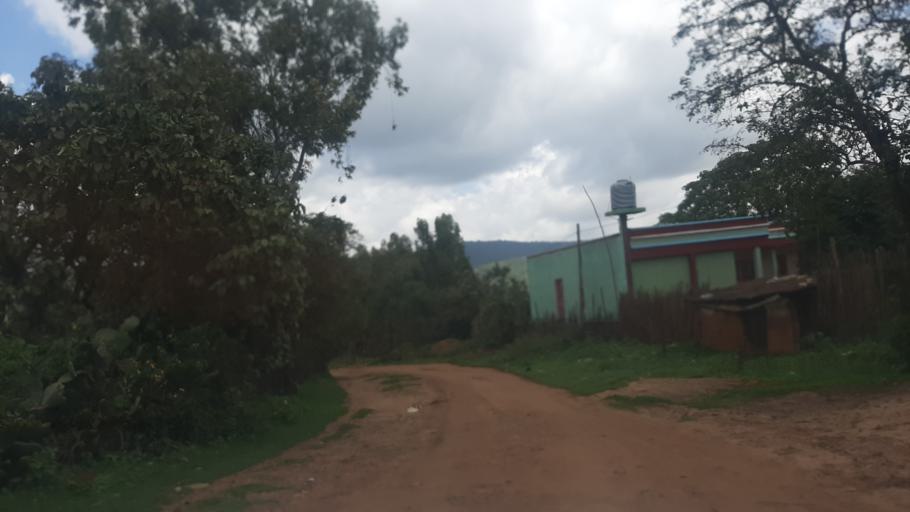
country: ET
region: Oromiya
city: Yabelo
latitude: 4.8911
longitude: 38.0820
